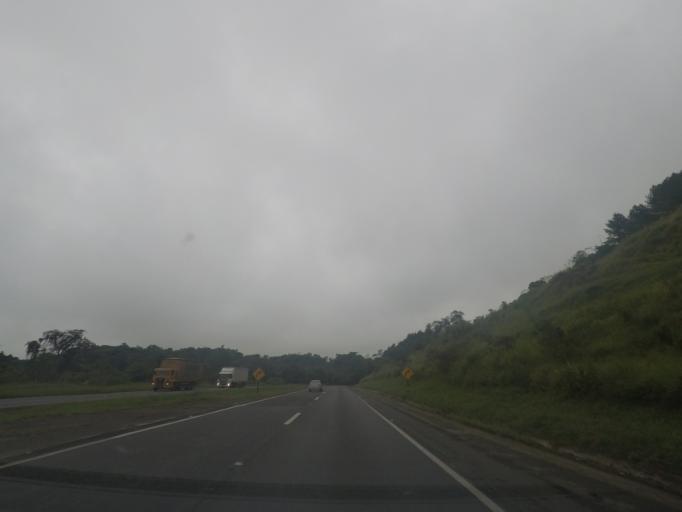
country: BR
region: Parana
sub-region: Antonina
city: Antonina
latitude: -25.0712
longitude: -48.5854
